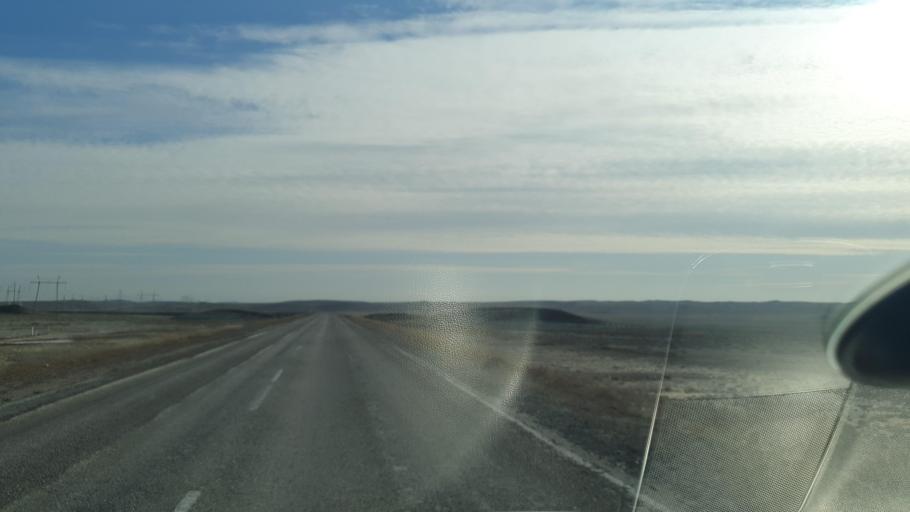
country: KZ
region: Zhambyl
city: Mynaral
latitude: 45.5691
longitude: 73.4183
